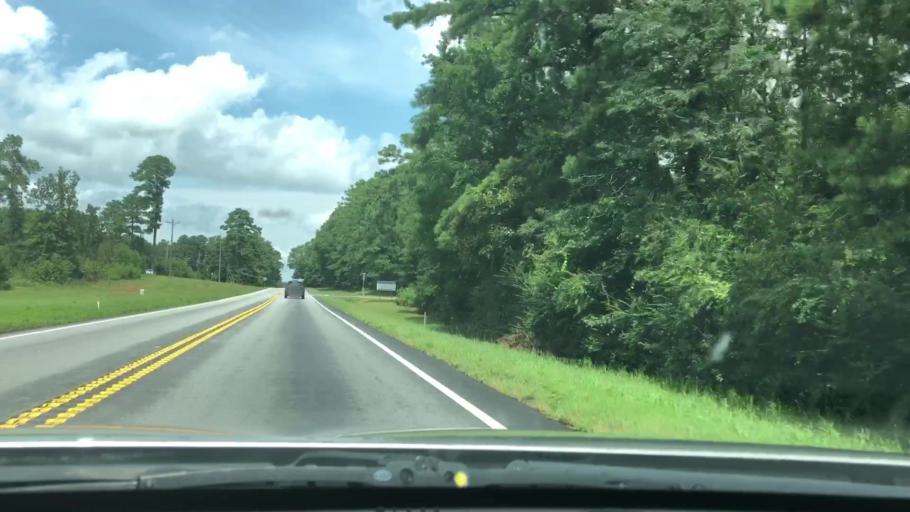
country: US
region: Georgia
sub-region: Lamar County
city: Barnesville
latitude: 33.1119
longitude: -84.1544
